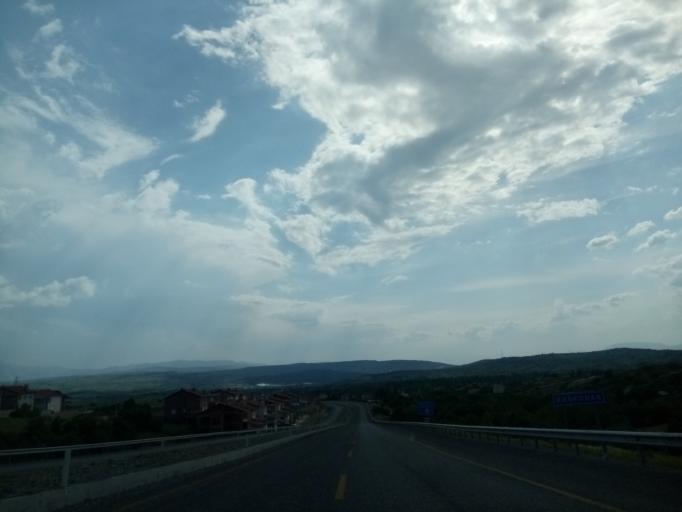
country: TR
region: Isparta
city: Bagkonak
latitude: 38.2165
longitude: 31.2842
